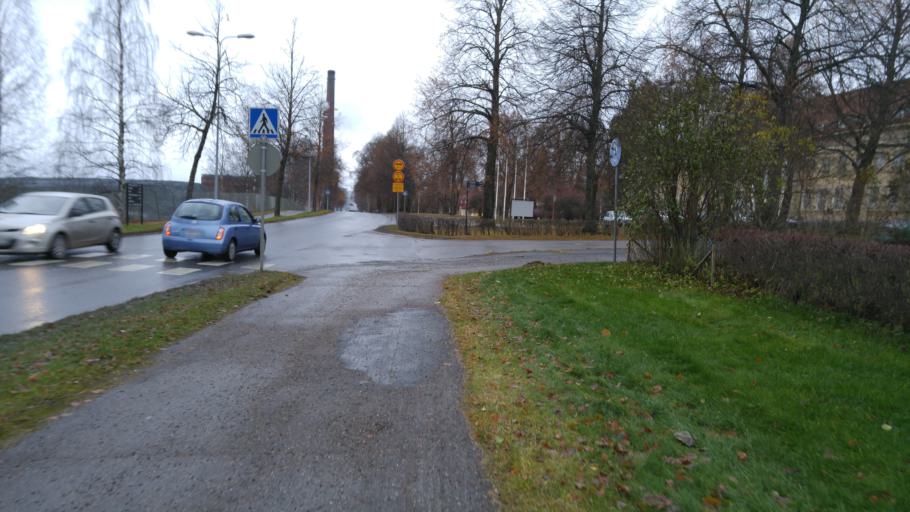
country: FI
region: Pirkanmaa
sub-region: Ylae-Pirkanmaa
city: Maenttae
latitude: 62.0271
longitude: 24.6459
